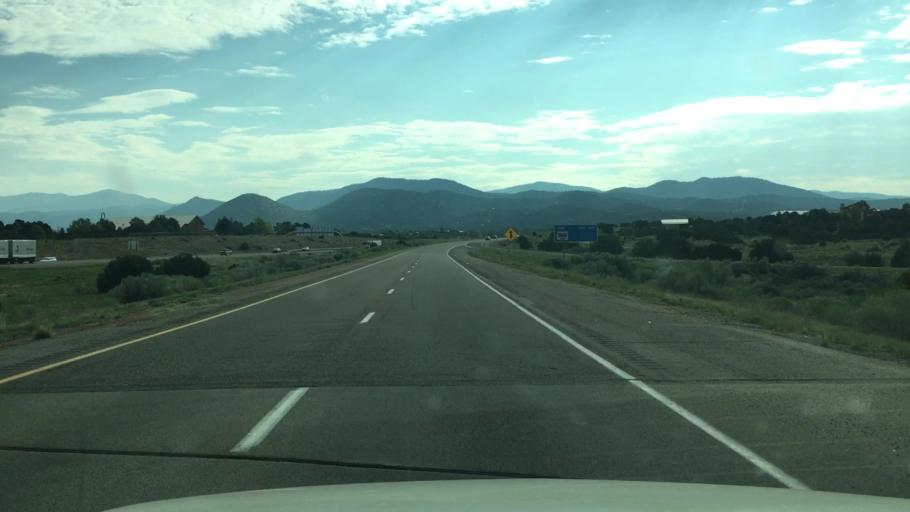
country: US
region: New Mexico
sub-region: Santa Fe County
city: Santa Fe
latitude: 35.6351
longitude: -105.9540
